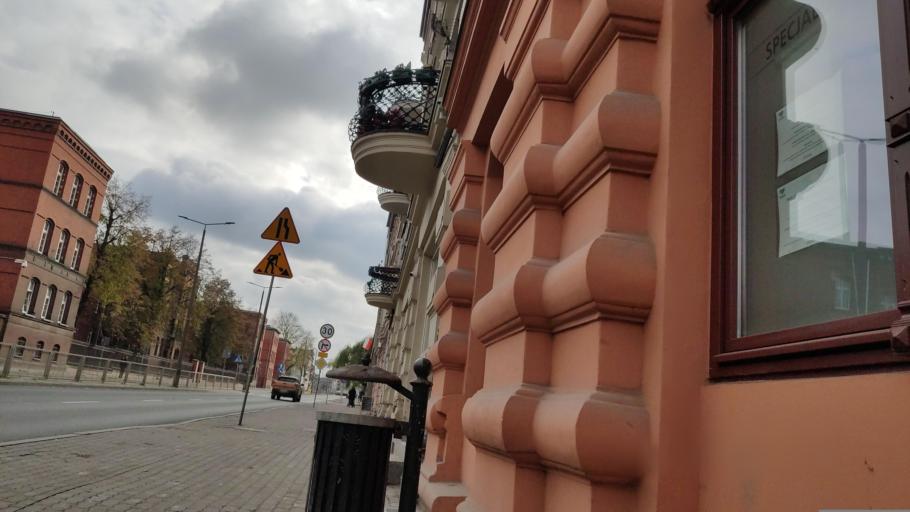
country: PL
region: Kujawsko-Pomorskie
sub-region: Powiat inowroclawski
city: Inowroclaw
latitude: 52.8043
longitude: 18.2488
